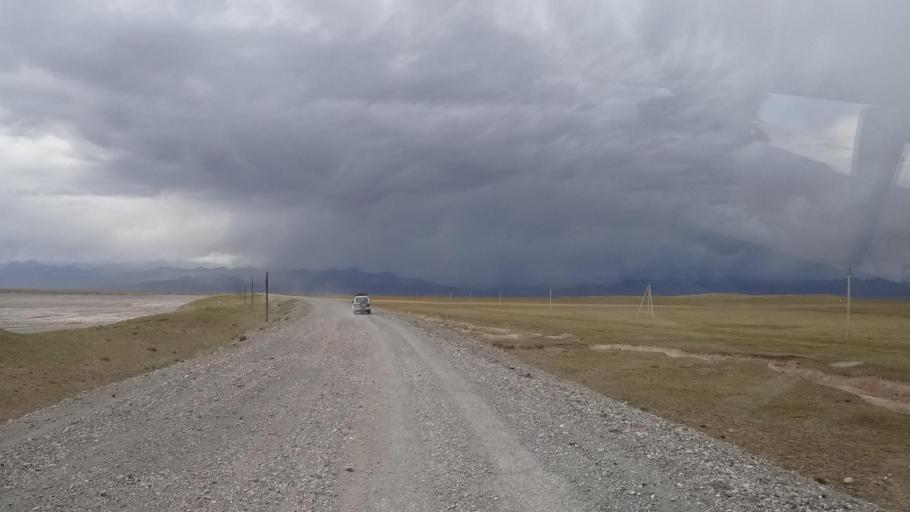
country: KG
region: Osh
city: Gul'cha
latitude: 39.5744
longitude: 73.2578
